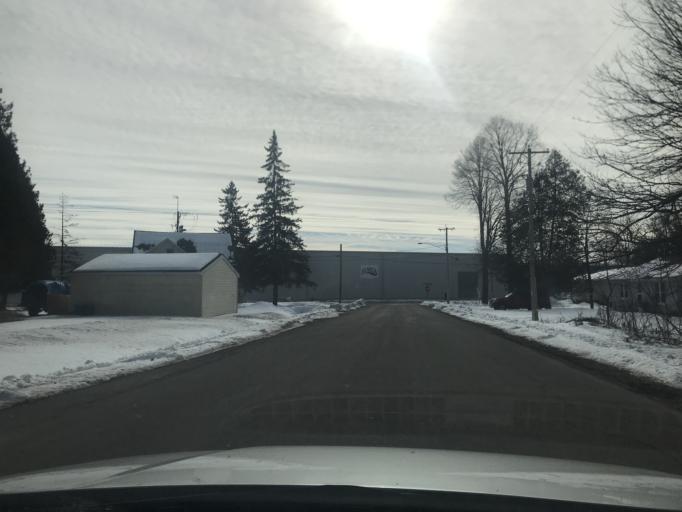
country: US
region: Wisconsin
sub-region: Oconto County
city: Gillett
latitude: 44.8957
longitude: -88.2972
